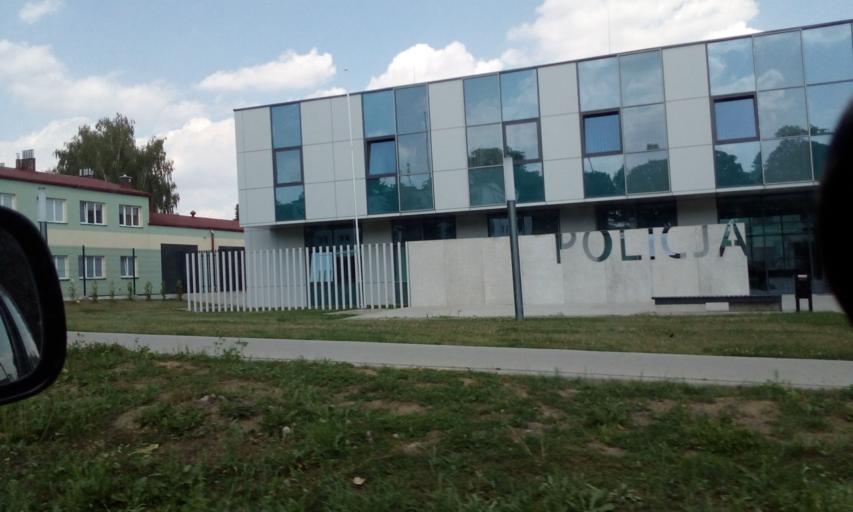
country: PL
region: Subcarpathian Voivodeship
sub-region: Powiat lancucki
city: Lancut
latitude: 50.0603
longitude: 22.2302
